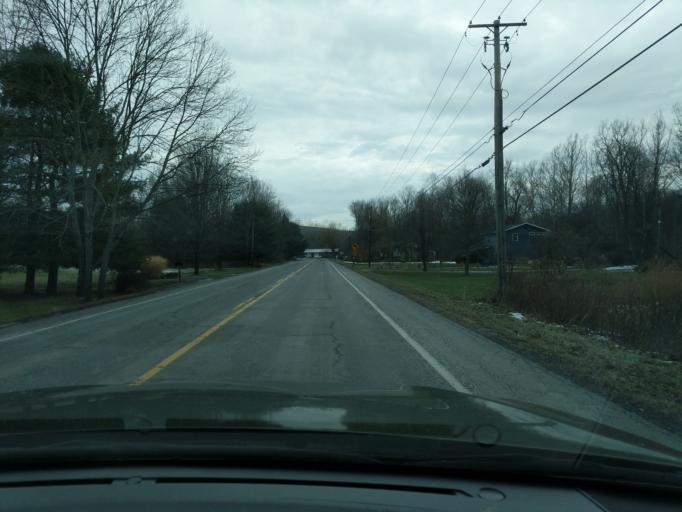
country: US
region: New York
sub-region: Tompkins County
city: East Ithaca
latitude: 42.3921
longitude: -76.4162
